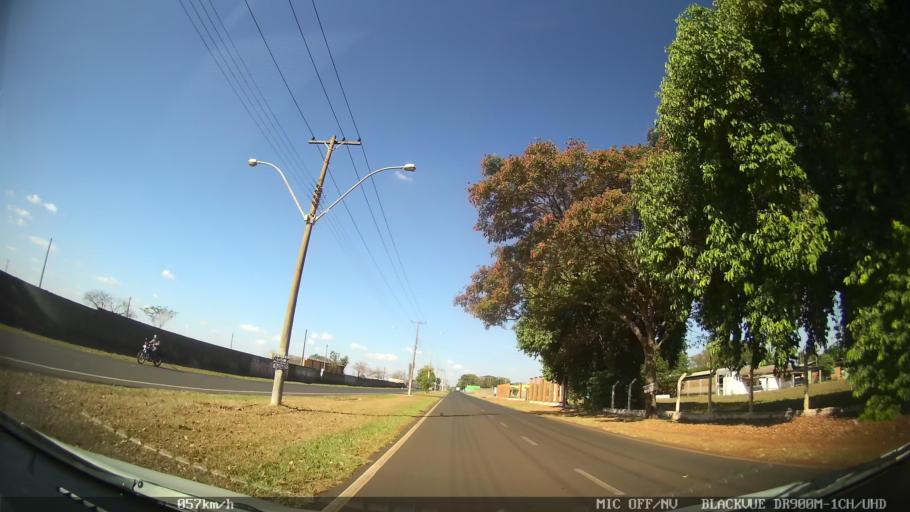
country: BR
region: Sao Paulo
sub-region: Ribeirao Preto
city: Ribeirao Preto
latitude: -21.1498
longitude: -47.7688
